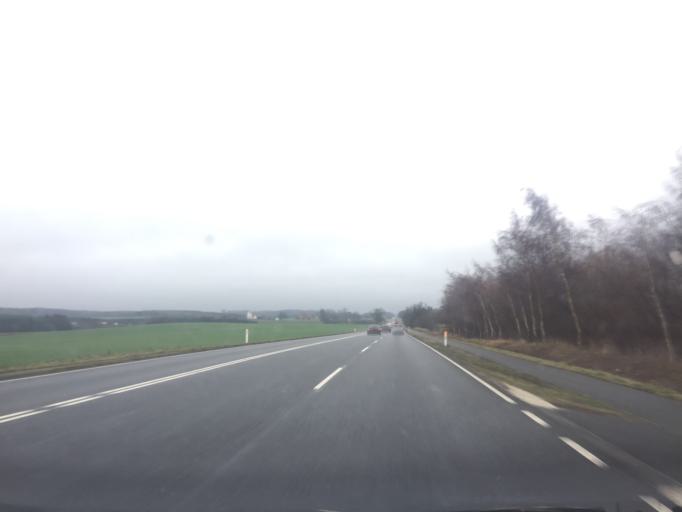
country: DK
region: Zealand
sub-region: Soro Kommune
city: Soro
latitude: 55.4275
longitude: 11.4585
